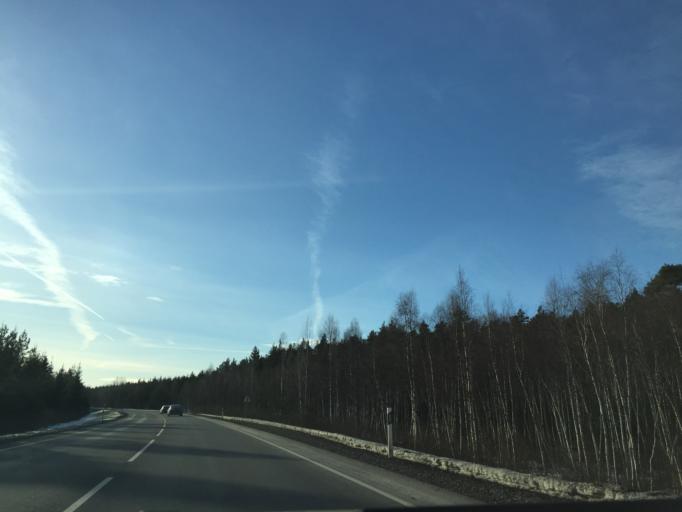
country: EE
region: Saare
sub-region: Kuressaare linn
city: Kuressaare
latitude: 58.3510
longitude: 22.6873
